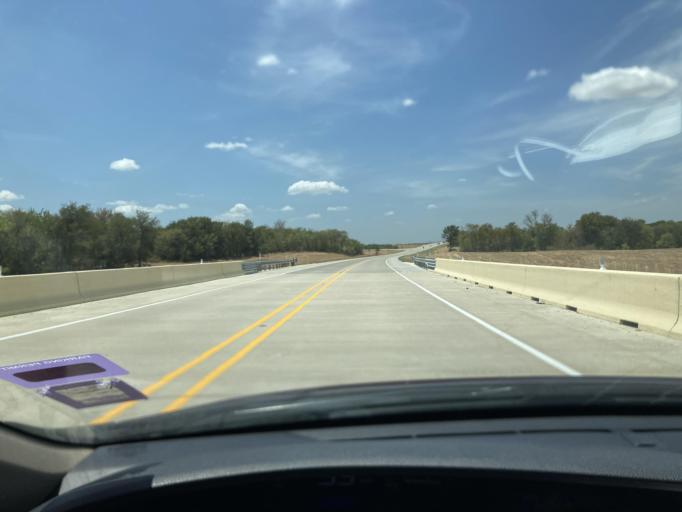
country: US
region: Texas
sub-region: Navarro County
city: Corsicana
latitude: 32.0543
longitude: -96.4129
